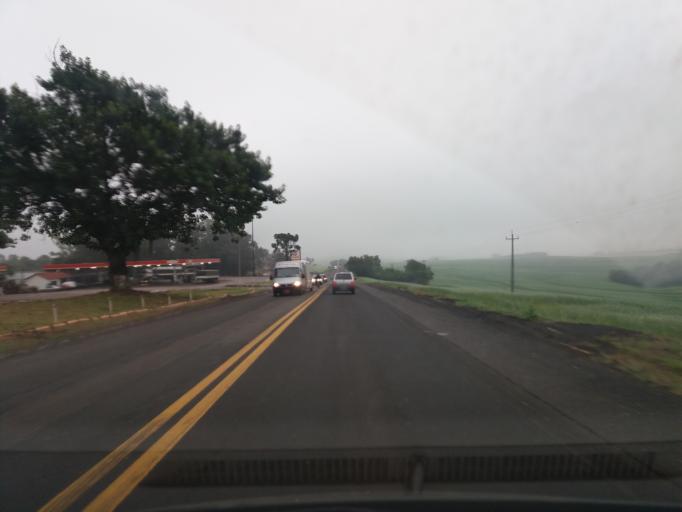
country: BR
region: Parana
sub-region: Realeza
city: Realeza
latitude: -25.8155
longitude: -53.5197
